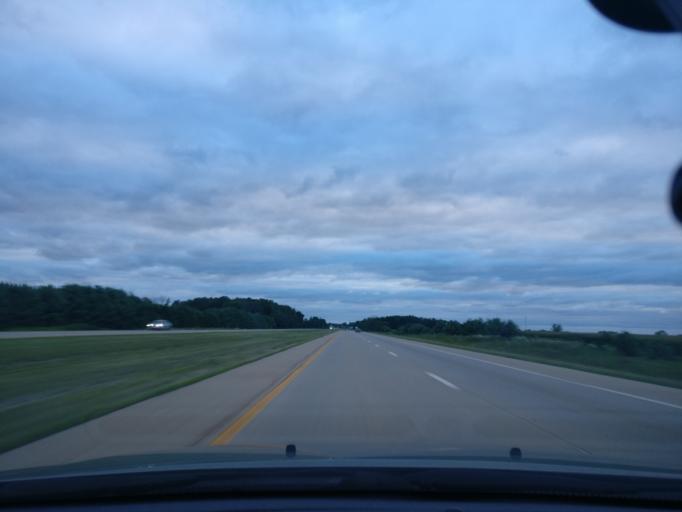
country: US
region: Ohio
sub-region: Greene County
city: Wilberforce
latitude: 39.6881
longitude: -83.8608
